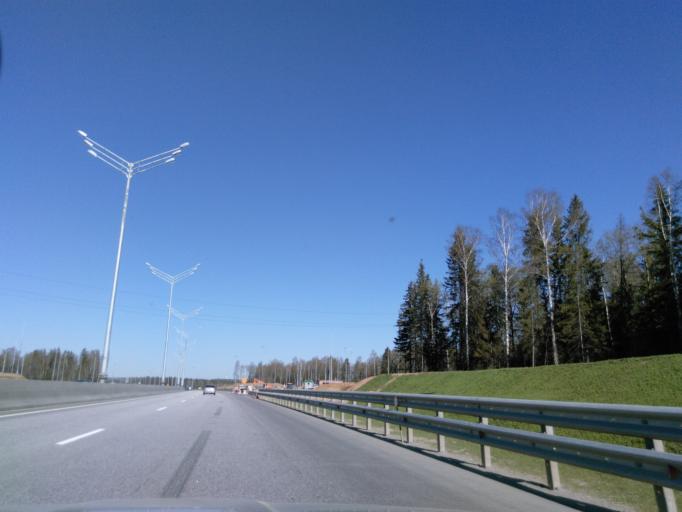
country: RU
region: Moskovskaya
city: Radumlya
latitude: 56.0953
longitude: 37.1890
